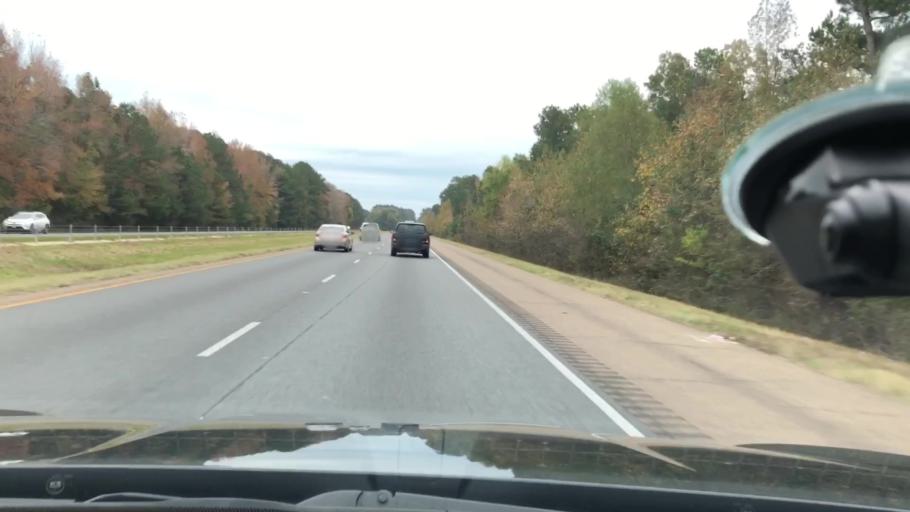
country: US
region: Arkansas
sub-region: Clark County
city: Gurdon
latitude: 33.9117
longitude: -93.2852
